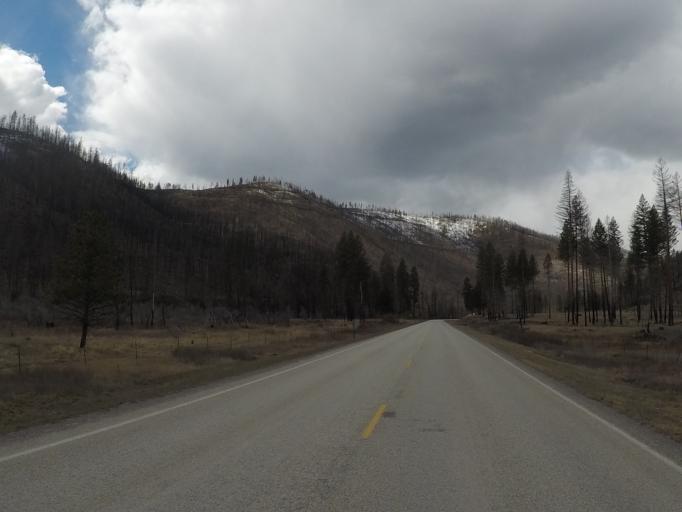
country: US
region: Montana
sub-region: Missoula County
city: Lolo
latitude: 46.7586
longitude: -114.3084
